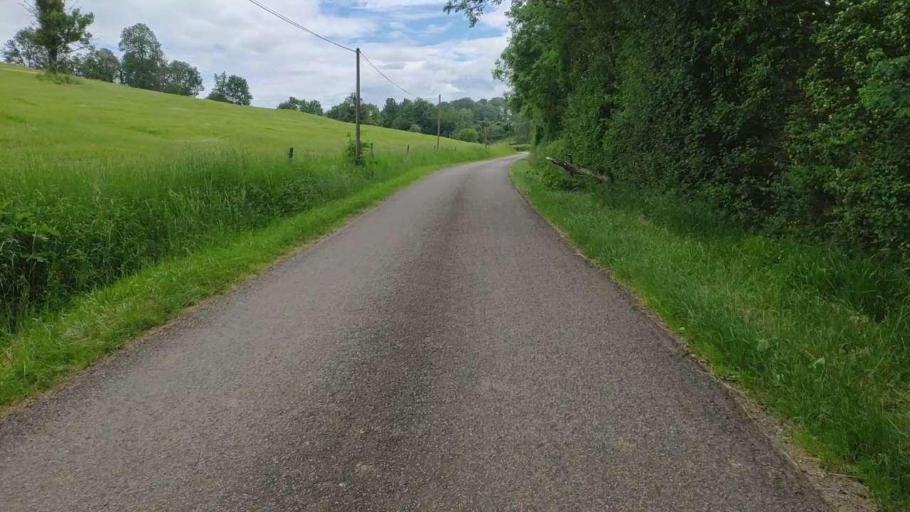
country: FR
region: Franche-Comte
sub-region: Departement du Jura
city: Montmorot
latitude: 46.7531
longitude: 5.5541
